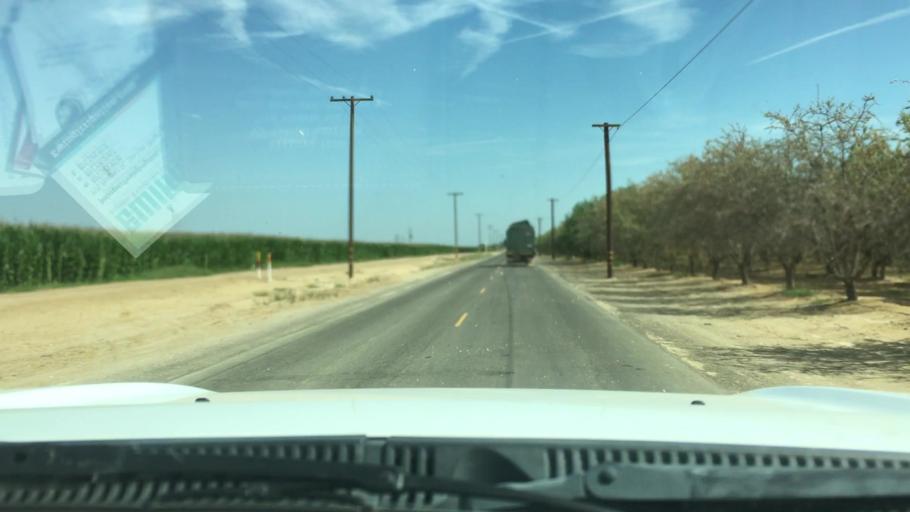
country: US
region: California
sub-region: Kern County
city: Shafter
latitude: 35.4755
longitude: -119.3680
